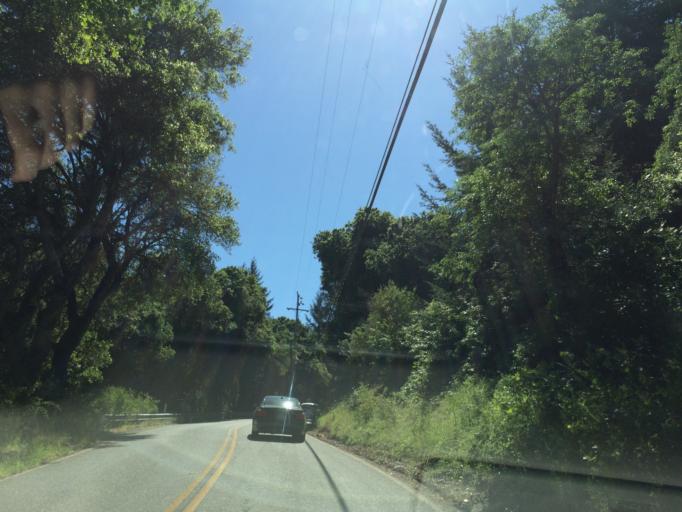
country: US
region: California
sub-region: Santa Clara County
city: Lexington Hills
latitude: 37.1737
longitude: -122.0118
